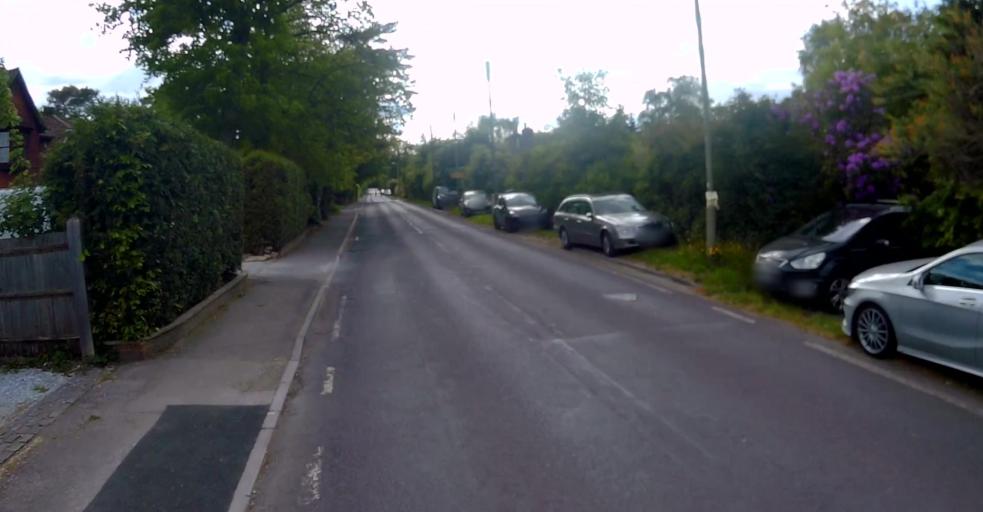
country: GB
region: England
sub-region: Hampshire
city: Fleet
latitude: 51.2894
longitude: -0.8429
